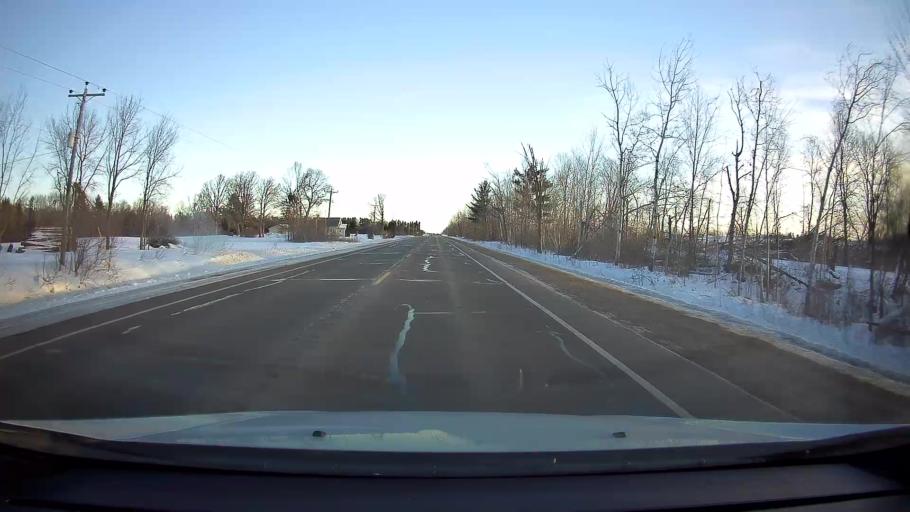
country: US
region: Wisconsin
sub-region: Barron County
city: Cumberland
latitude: 45.4825
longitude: -92.0687
